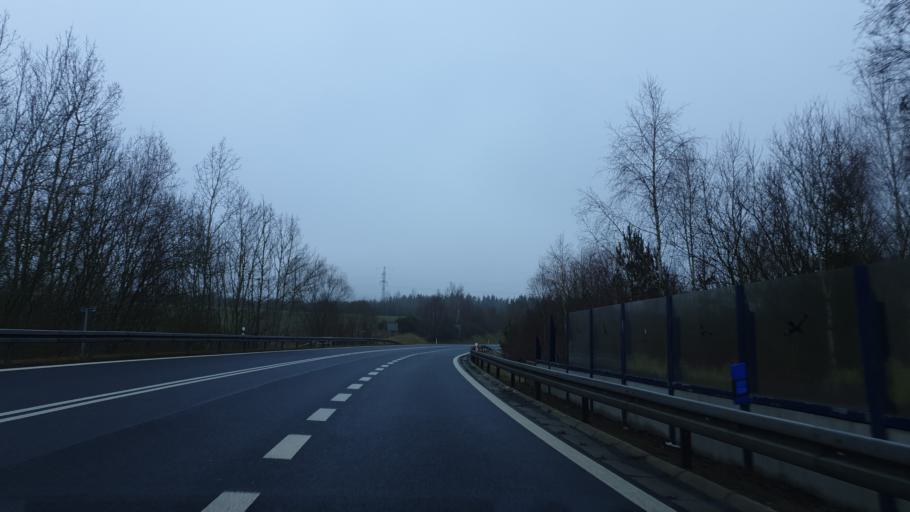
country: CZ
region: Karlovarsky
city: Hazlov
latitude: 50.1680
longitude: 12.3142
